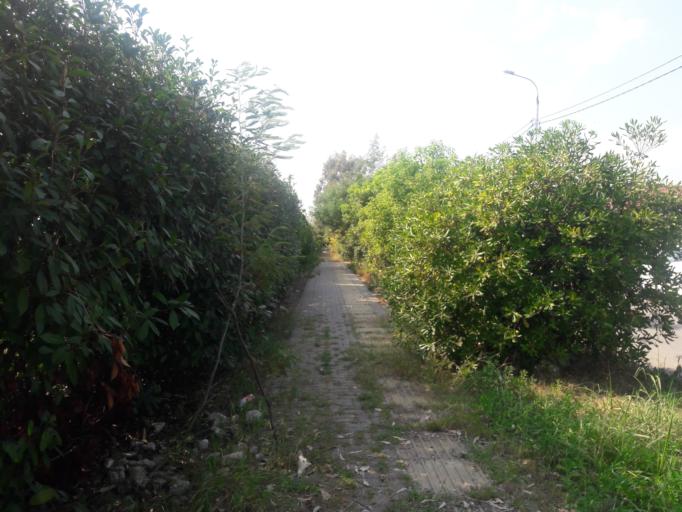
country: RU
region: Krasnodarskiy
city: Vysokoye
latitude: 43.3938
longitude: 39.9986
